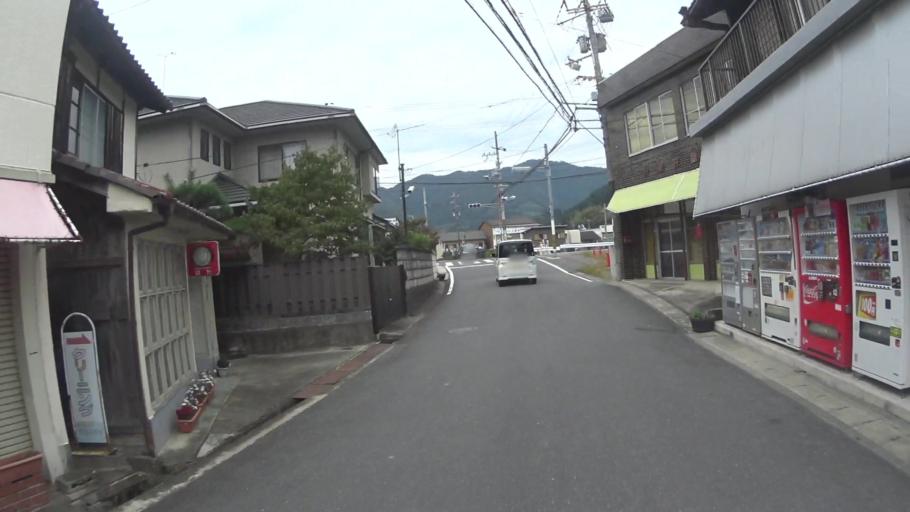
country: JP
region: Kyoto
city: Uji
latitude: 34.7955
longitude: 135.9040
